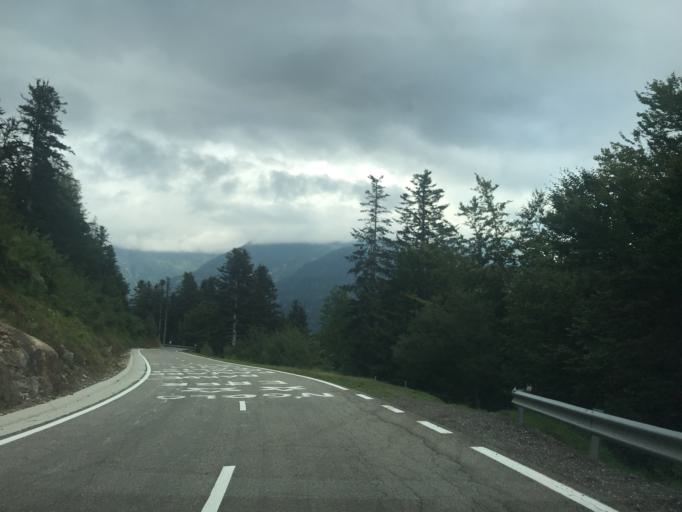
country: ES
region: Catalonia
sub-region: Provincia de Lleida
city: Les
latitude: 42.7660
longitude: 0.6647
